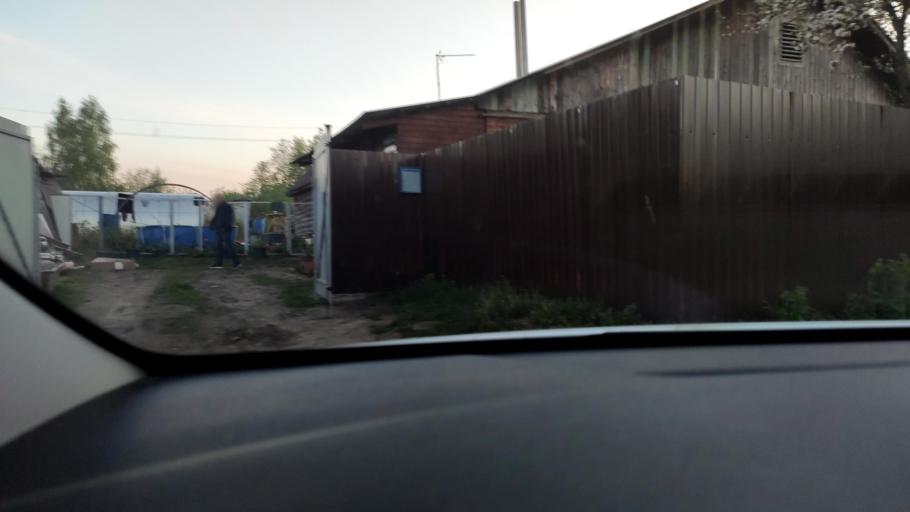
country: RU
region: Tatarstan
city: Stolbishchi
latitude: 55.7377
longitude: 49.2712
